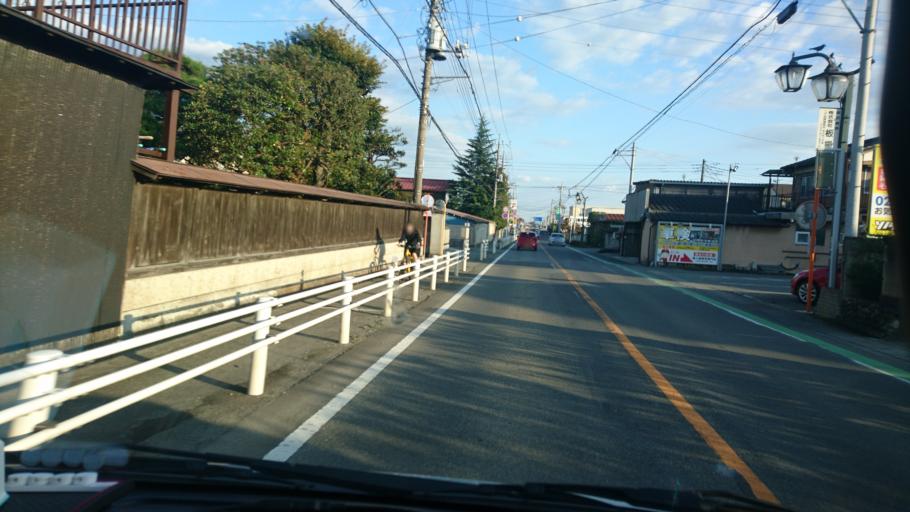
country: JP
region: Gunma
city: Kiryu
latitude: 36.4098
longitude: 139.3114
